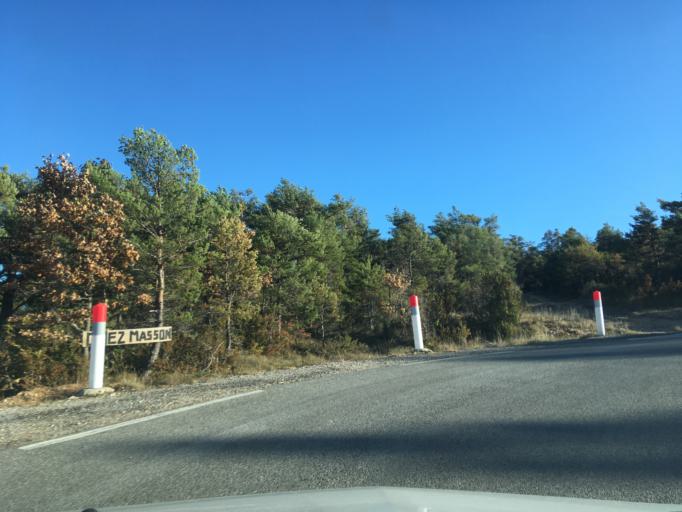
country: FR
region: Provence-Alpes-Cote d'Azur
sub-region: Departement des Alpes-de-Haute-Provence
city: Castellane
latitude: 43.7488
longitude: 6.4373
